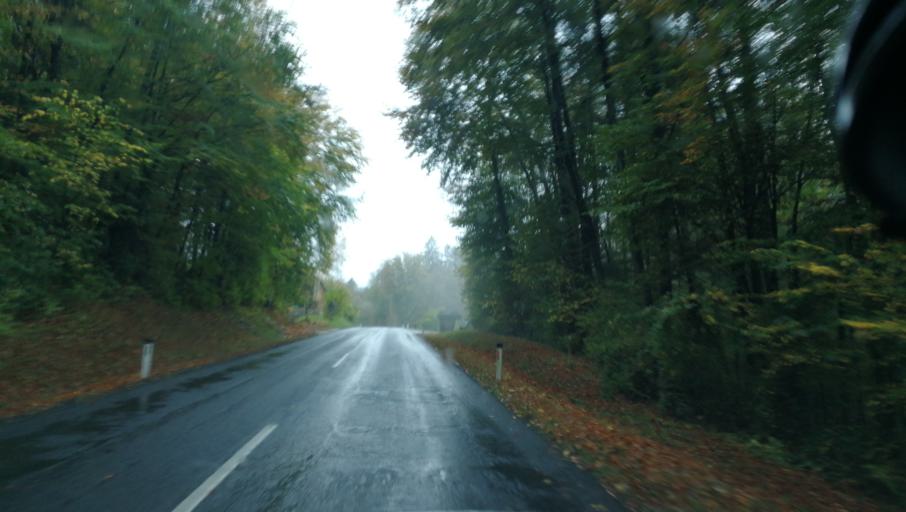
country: AT
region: Styria
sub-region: Politischer Bezirk Leibnitz
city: Spielfeld
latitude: 46.7007
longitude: 15.6173
